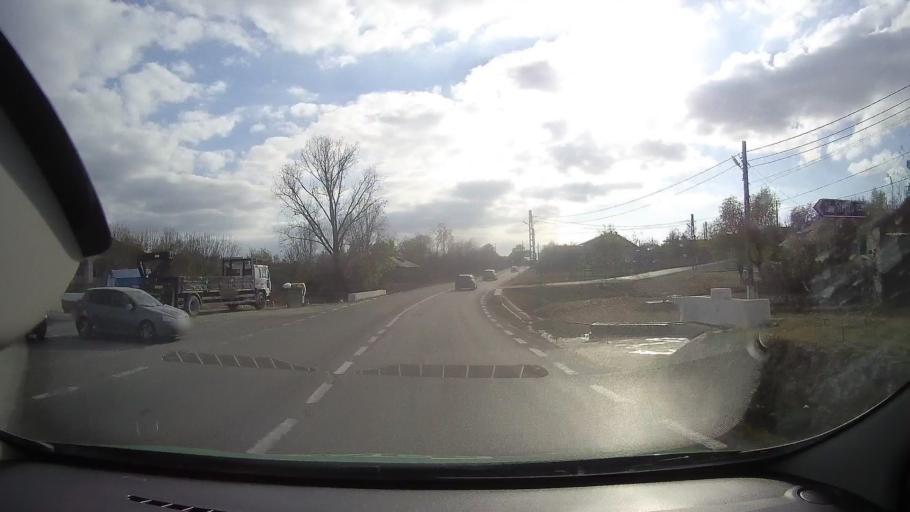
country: RO
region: Tulcea
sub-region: Comuna Topolog
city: Topolog
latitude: 44.8755
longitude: 28.3738
